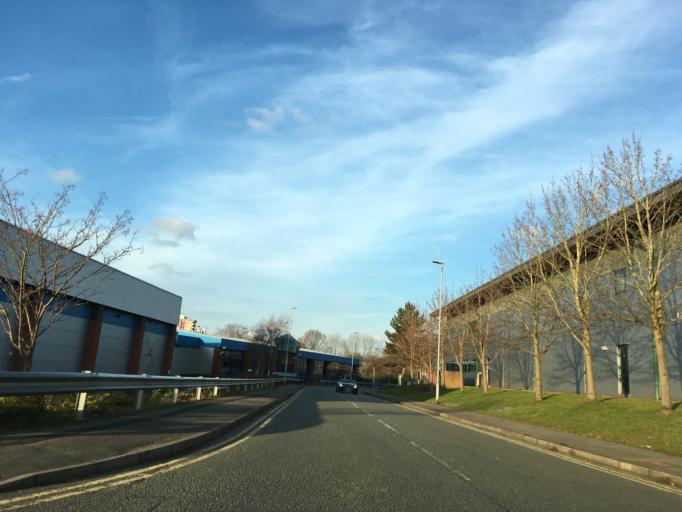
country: GB
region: England
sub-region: Borough of Stockport
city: Cheadle Hulme
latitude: 53.3511
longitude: -2.2088
